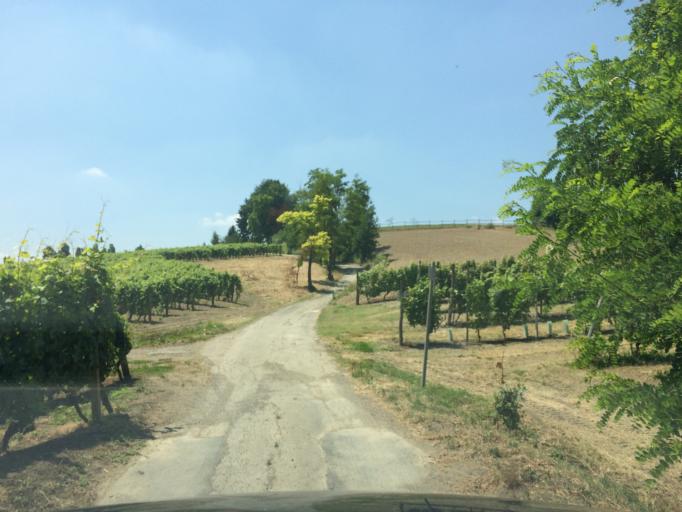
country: IT
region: Piedmont
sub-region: Provincia di Asti
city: Moasca
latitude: 44.7640
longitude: 8.2621
